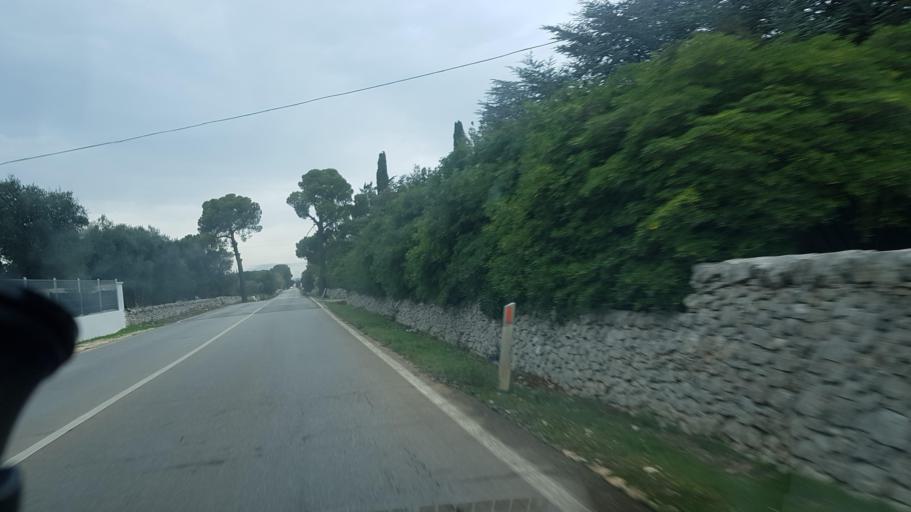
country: IT
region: Apulia
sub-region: Provincia di Brindisi
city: Carovigno
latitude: 40.7088
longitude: 17.6420
